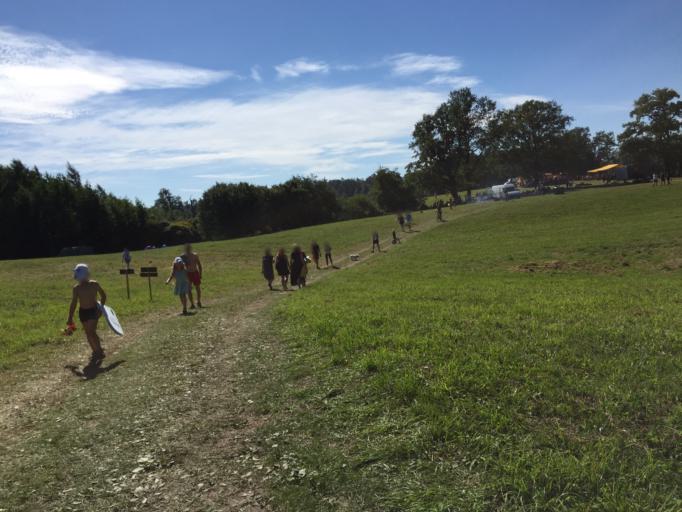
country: LT
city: Zarasai
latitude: 55.7884
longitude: 25.9652
